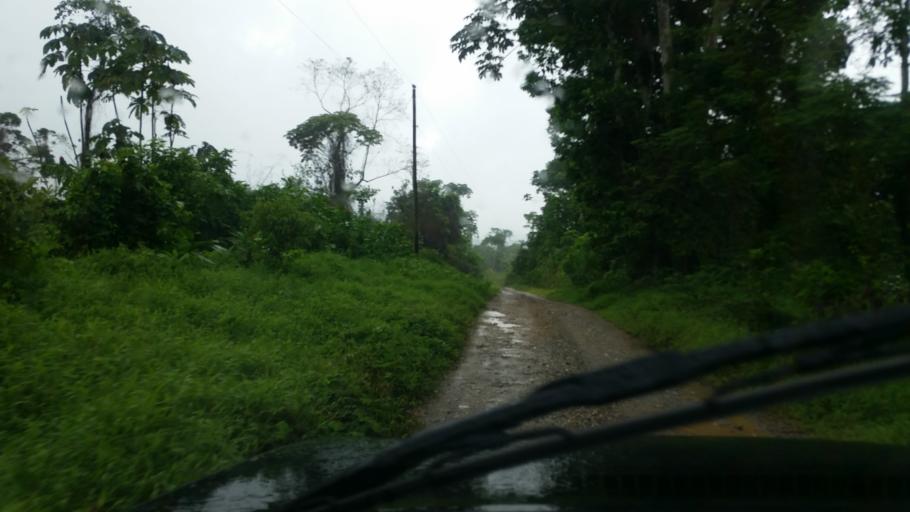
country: NI
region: Atlantico Norte (RAAN)
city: Bonanza
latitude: 14.0762
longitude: -84.6590
